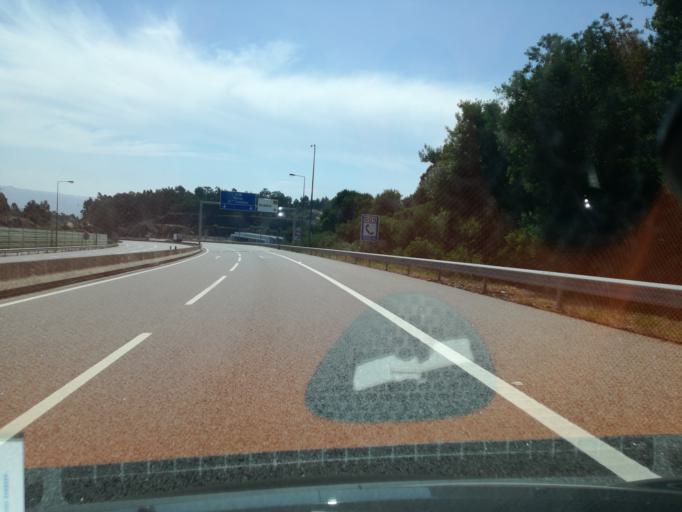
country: PT
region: Viana do Castelo
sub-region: Viana do Castelo
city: Meadela
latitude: 41.7447
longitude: -8.7989
